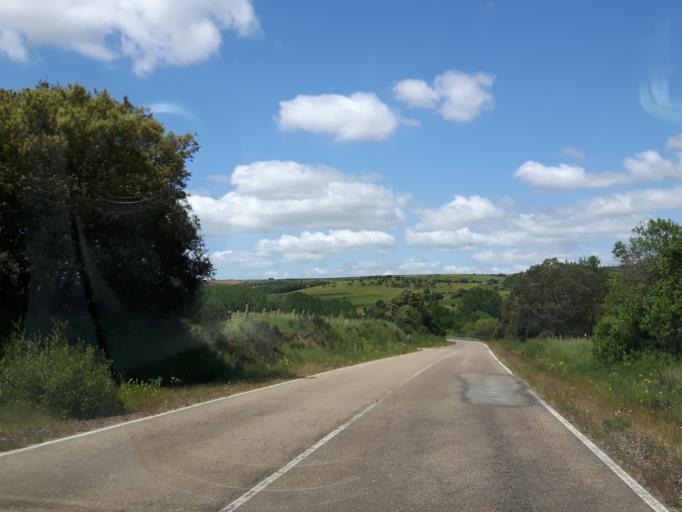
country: ES
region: Castille and Leon
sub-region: Provincia de Salamanca
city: Aldea del Obispo
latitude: 40.7205
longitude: -6.7776
